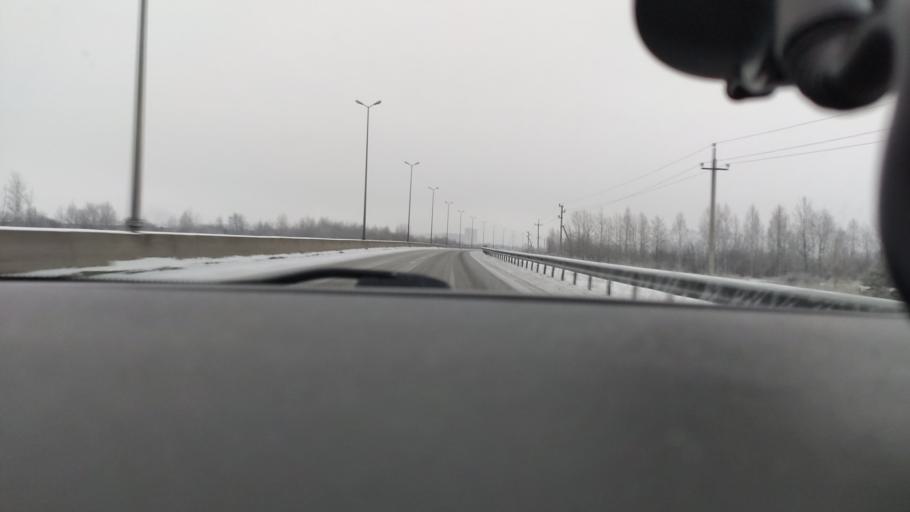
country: RU
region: Perm
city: Kondratovo
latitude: 58.0041
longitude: 56.0790
